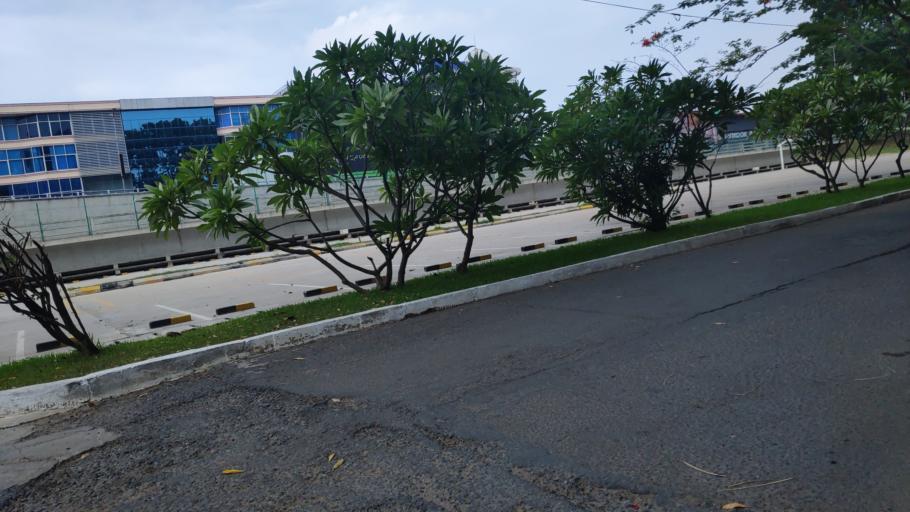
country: KH
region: Phnom Penh
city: Phnom Penh
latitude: 11.5702
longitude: 104.8991
